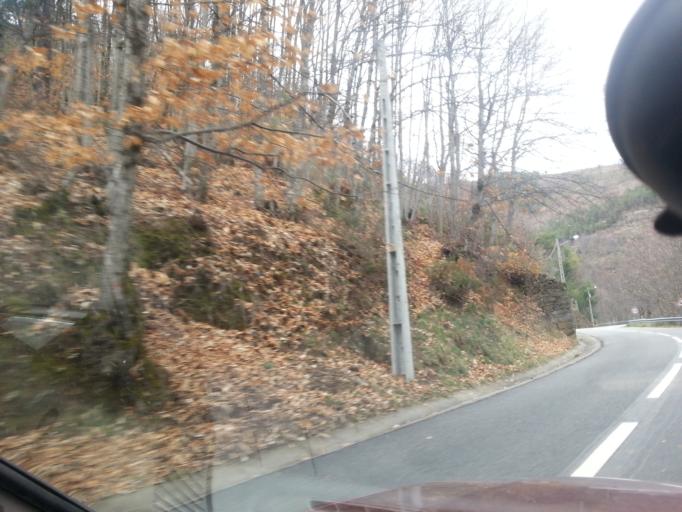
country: PT
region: Guarda
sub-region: Manteigas
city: Manteigas
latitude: 40.4085
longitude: -7.5273
